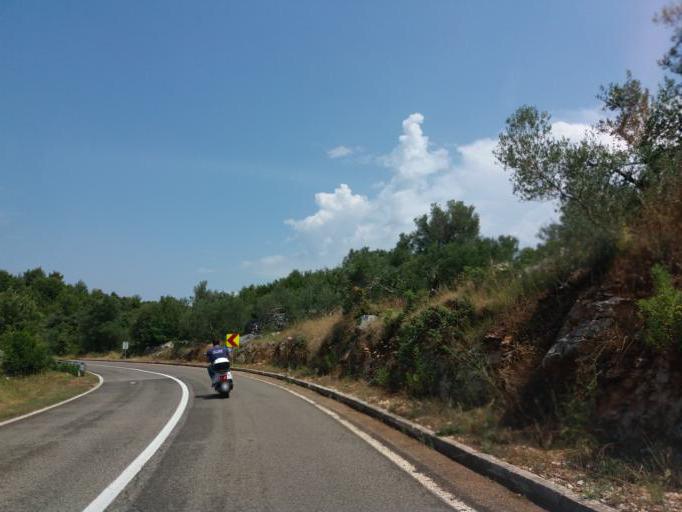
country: HR
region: Zadarska
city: Sali
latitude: 43.9393
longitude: 15.1428
